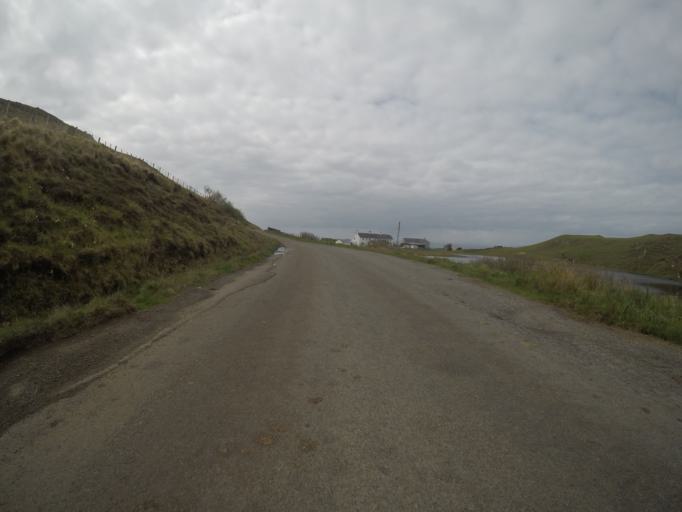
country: GB
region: Scotland
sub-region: Highland
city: Portree
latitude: 57.6830
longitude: -6.3342
